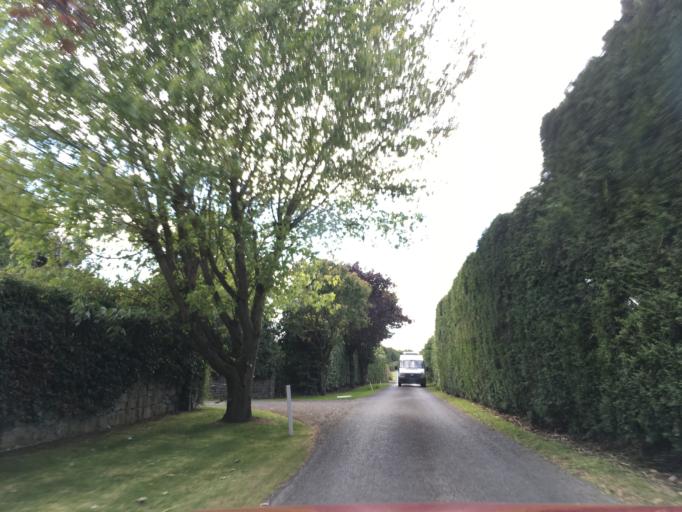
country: IE
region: Munster
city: Cashel
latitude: 52.4955
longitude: -7.9246
